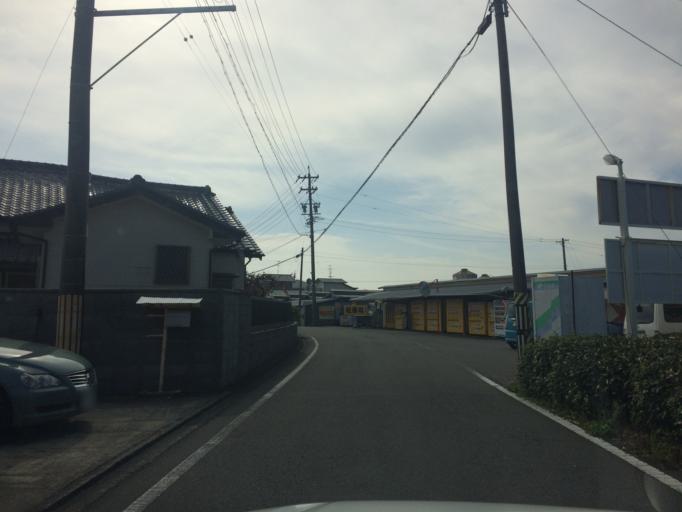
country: JP
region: Shizuoka
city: Yaizu
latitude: 34.8250
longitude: 138.3182
